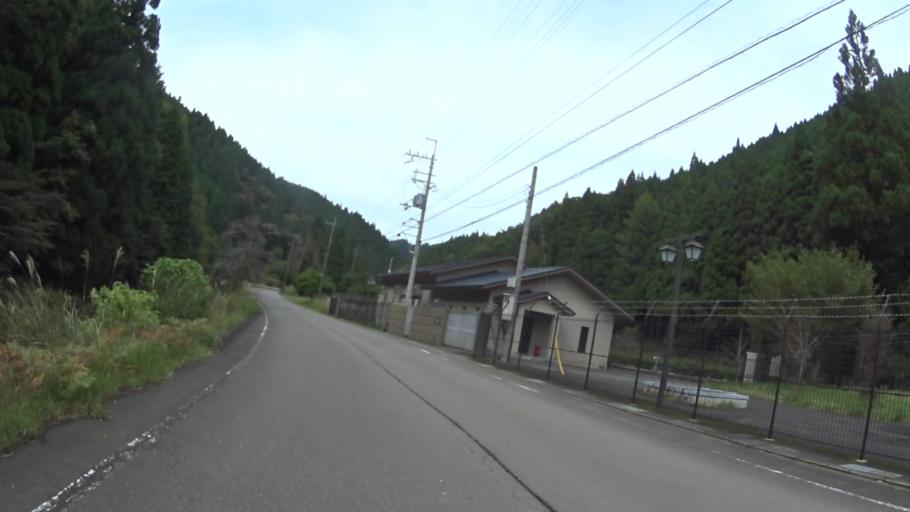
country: JP
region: Shiga Prefecture
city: Kitahama
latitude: 35.2646
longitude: 135.7454
